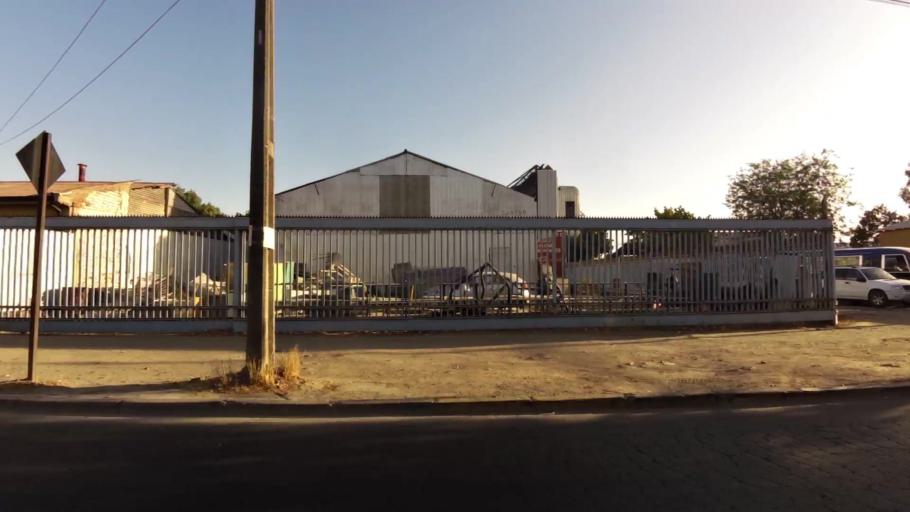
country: CL
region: Maule
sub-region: Provincia de Talca
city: Talca
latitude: -35.4318
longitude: -71.6466
